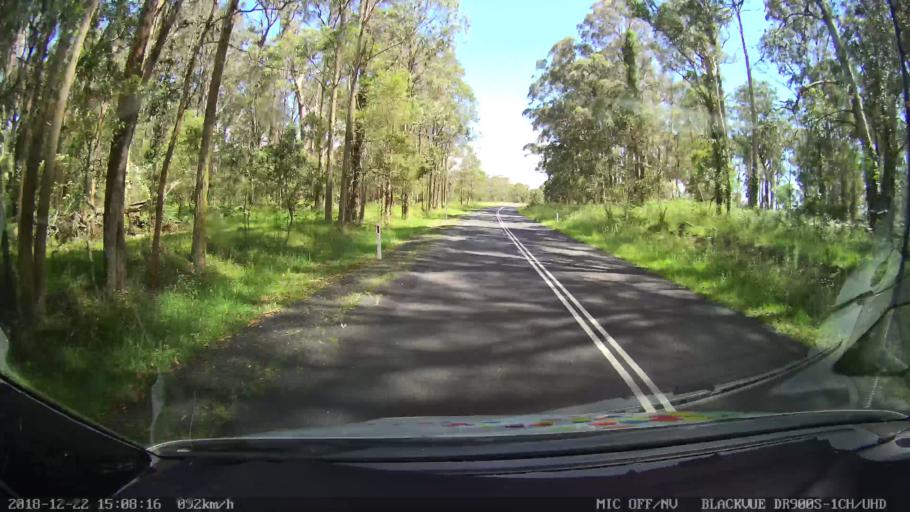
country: AU
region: New South Wales
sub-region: Bellingen
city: Dorrigo
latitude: -30.3102
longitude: 152.4140
